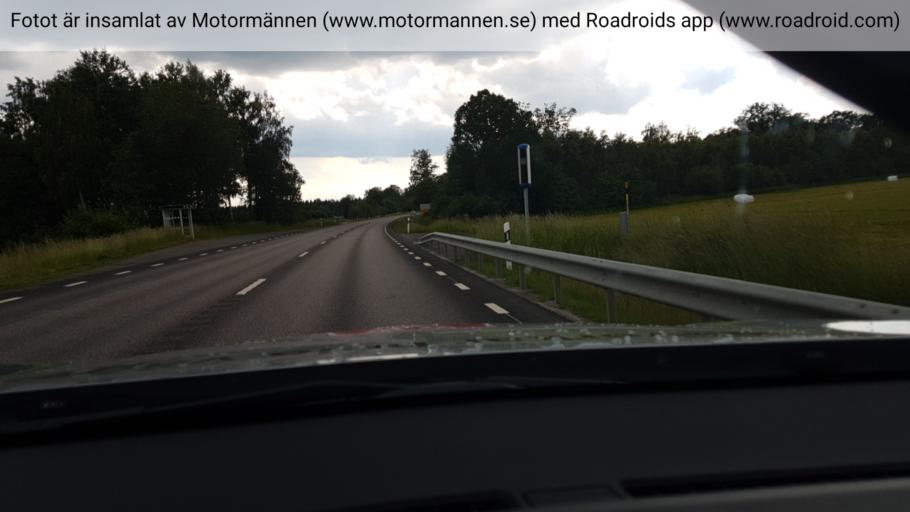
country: SE
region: Vaestra Goetaland
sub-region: Hjo Kommun
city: Hjo
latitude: 58.2659
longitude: 14.2580
